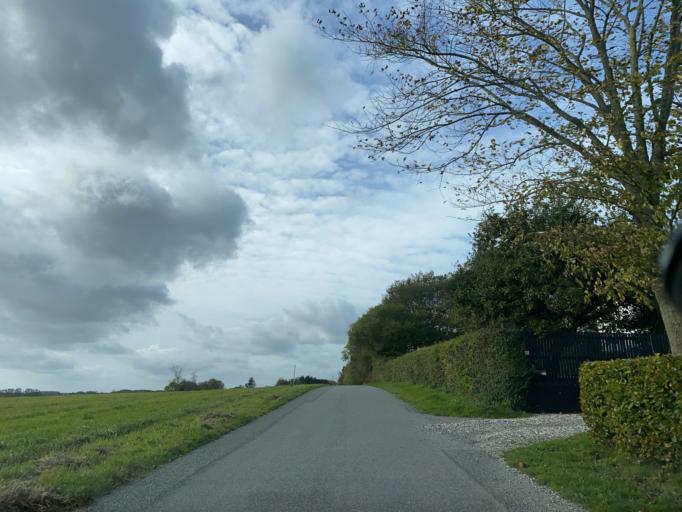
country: DK
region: Central Jutland
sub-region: Arhus Kommune
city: Sabro
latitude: 56.1964
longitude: 9.9956
